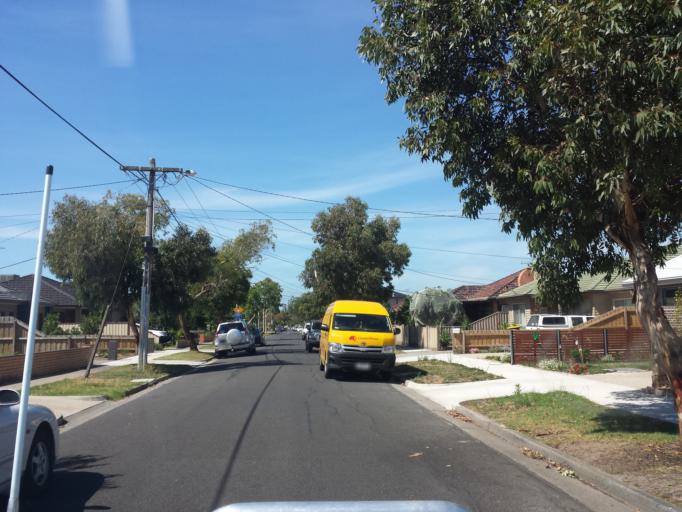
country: AU
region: Victoria
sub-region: Hobsons Bay
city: Altona North
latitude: -37.8342
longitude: 144.8549
